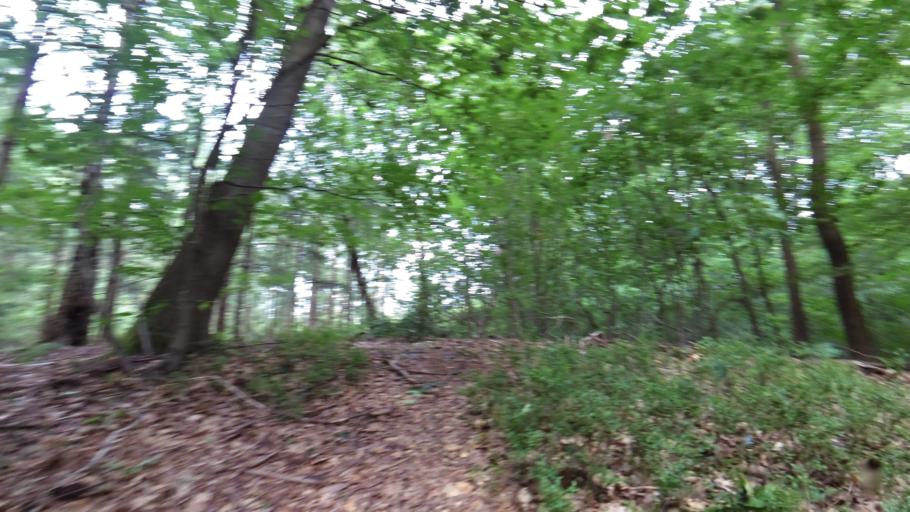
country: NL
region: Gelderland
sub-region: Gemeente Apeldoorn
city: Apeldoorn
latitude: 52.1910
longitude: 5.9132
